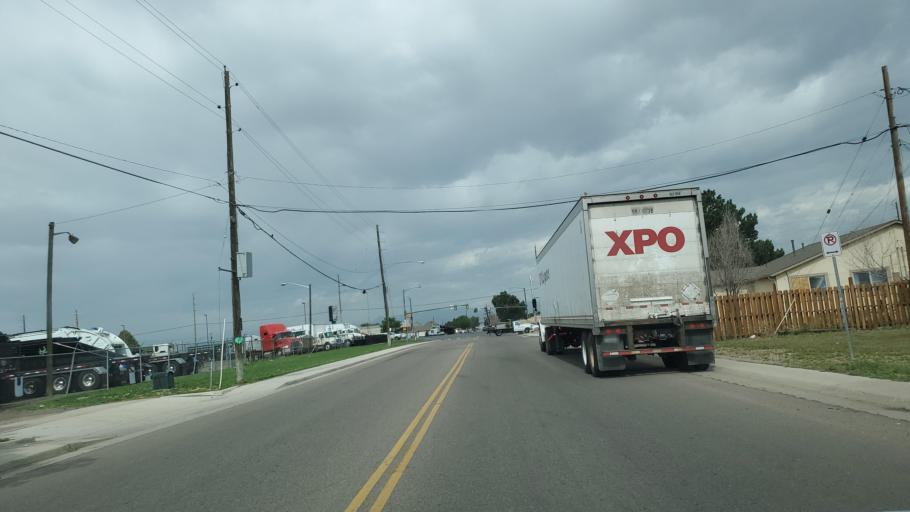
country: US
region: Colorado
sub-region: Adams County
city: Derby
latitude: 39.8364
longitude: -104.9224
